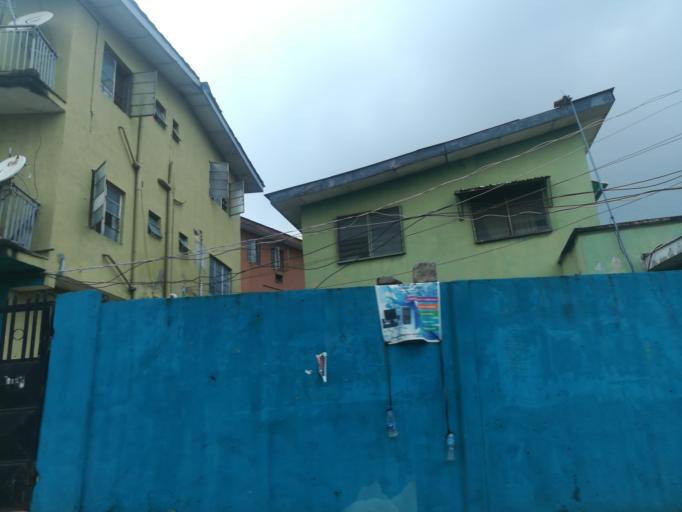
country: NG
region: Lagos
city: Ojota
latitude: 6.5710
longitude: 3.3736
